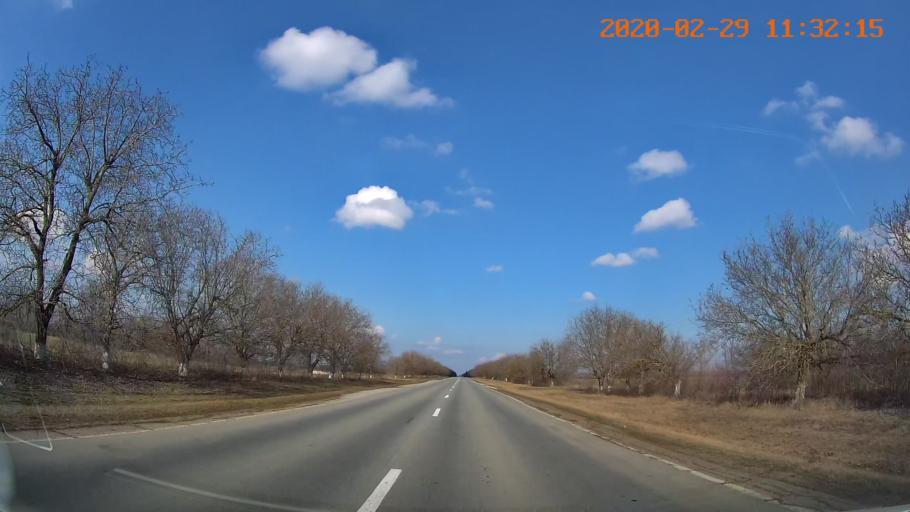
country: MD
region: Rezina
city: Saharna
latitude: 47.5354
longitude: 29.0963
